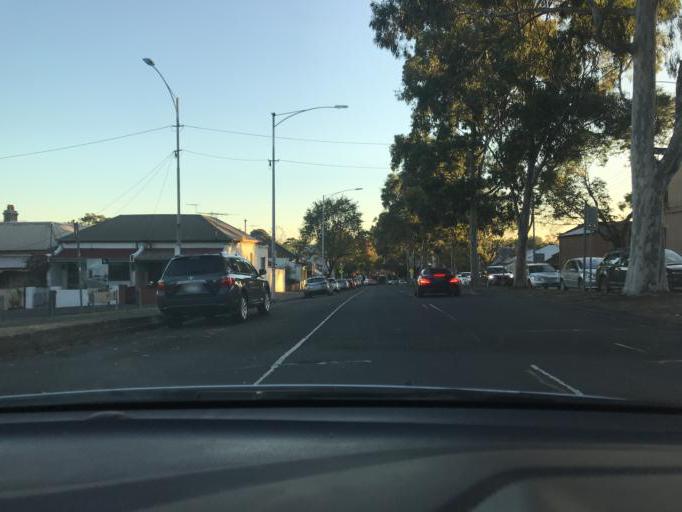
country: AU
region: Victoria
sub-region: Melbourne
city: North Melbourne
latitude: -37.7972
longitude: 144.9505
